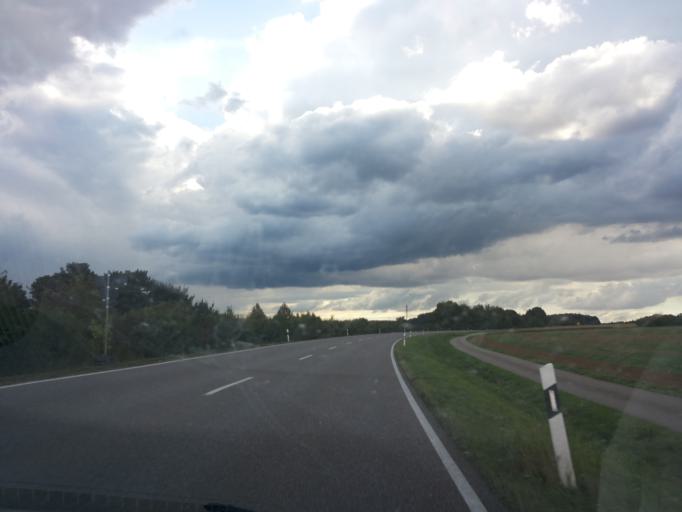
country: DE
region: Bavaria
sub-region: Upper Bavaria
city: Eitensheim
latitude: 48.8288
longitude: 11.3092
